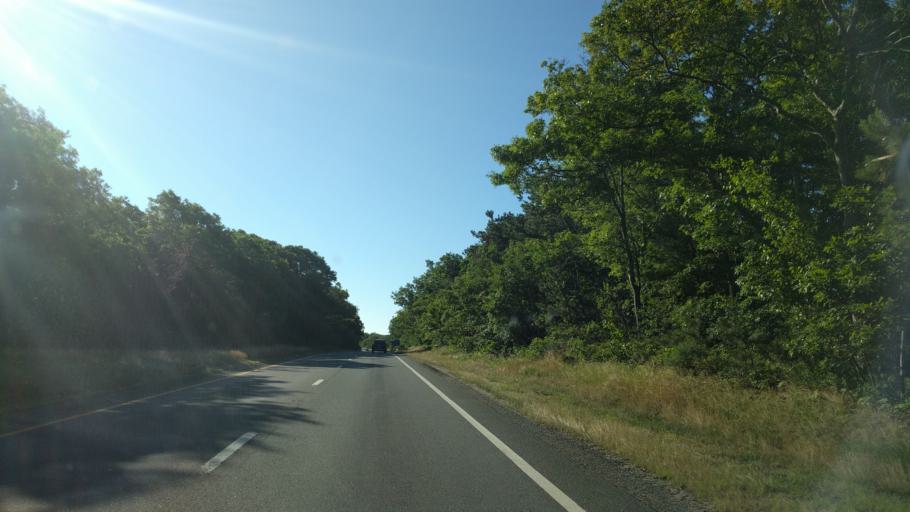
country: US
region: Massachusetts
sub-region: Barnstable County
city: West Barnstable
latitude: 41.6877
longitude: -70.3687
